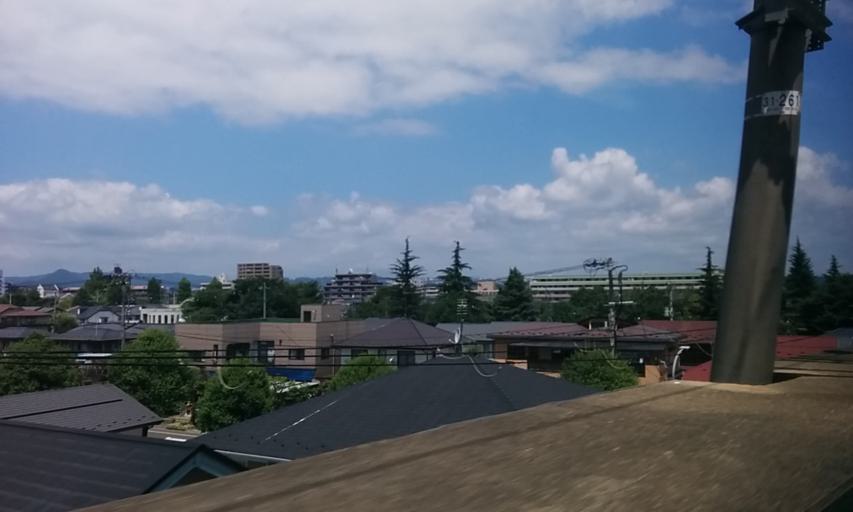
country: JP
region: Miyagi
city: Sendai
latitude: 38.1921
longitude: 140.8789
